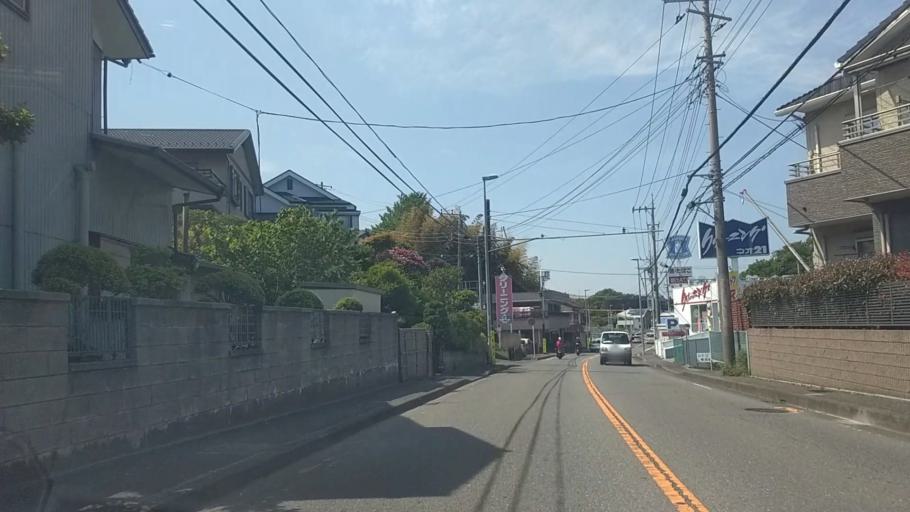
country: JP
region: Kanagawa
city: Kamakura
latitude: 35.3503
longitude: 139.5807
